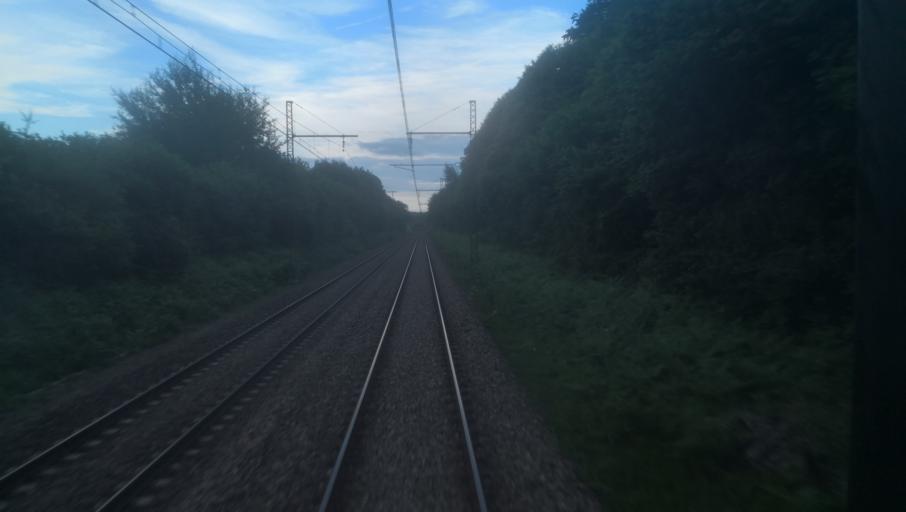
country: FR
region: Limousin
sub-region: Departement de la Creuse
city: Saint-Maurice-la-Souterraine
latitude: 46.1934
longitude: 1.4675
